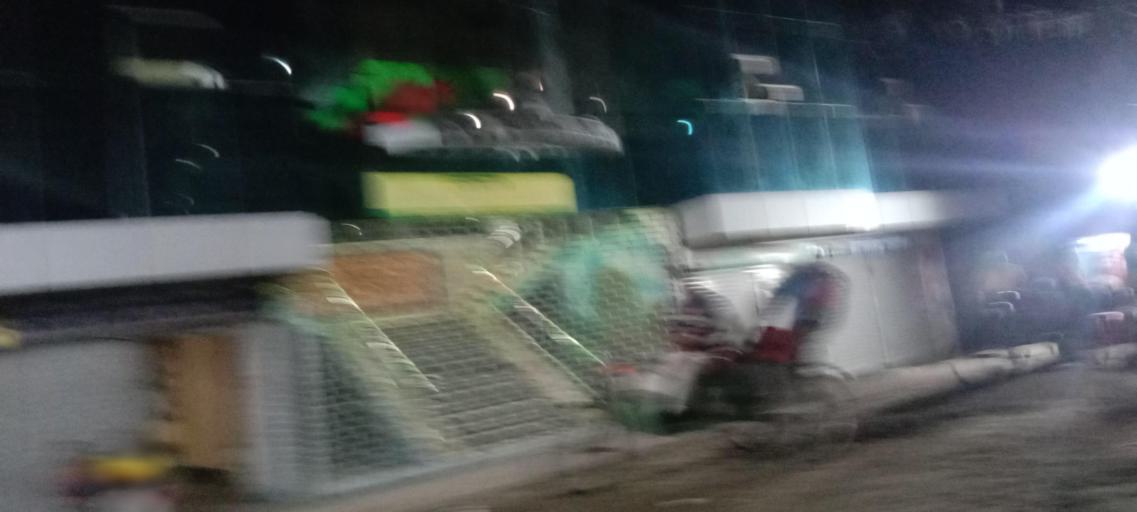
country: BD
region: Dhaka
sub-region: Dhaka
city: Dhaka
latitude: 23.7001
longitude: 90.3818
